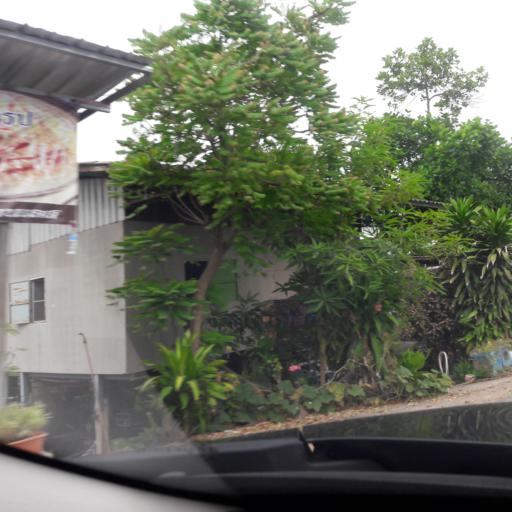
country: TH
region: Ratchaburi
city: Damnoen Saduak
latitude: 13.5577
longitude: 99.9658
